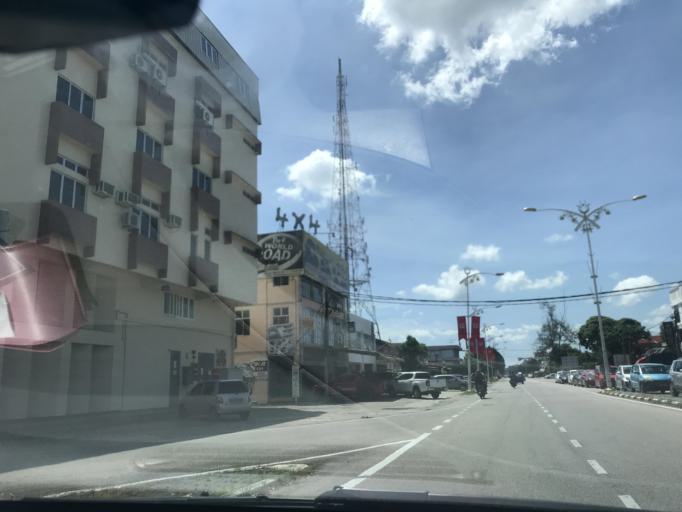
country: MY
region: Kelantan
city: Kota Bharu
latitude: 6.1092
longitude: 102.2416
